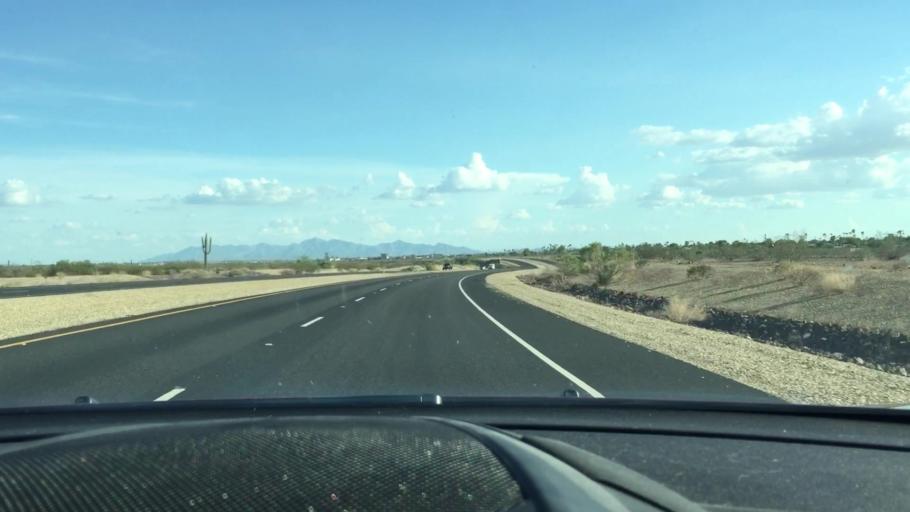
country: US
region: Arizona
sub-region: Maricopa County
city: Sun City West
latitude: 33.6689
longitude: -112.3230
